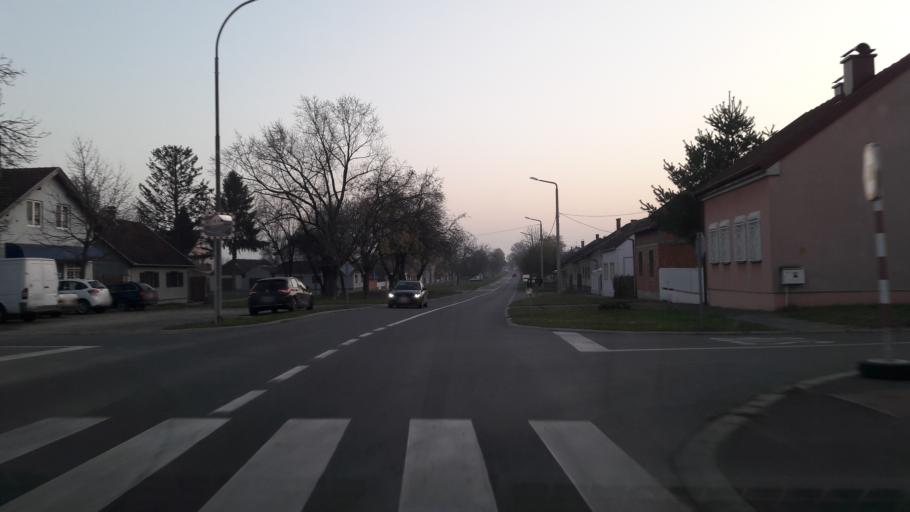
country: HR
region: Vukovarsko-Srijemska
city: Vukovar
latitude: 45.3396
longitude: 19.0029
